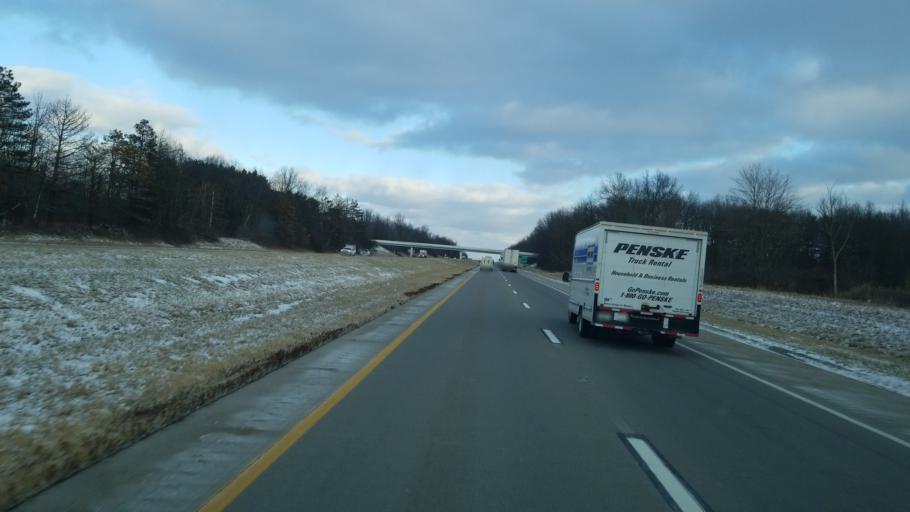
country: US
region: Ohio
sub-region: Mahoning County
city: Craig Beach
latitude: 41.1056
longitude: -80.9100
